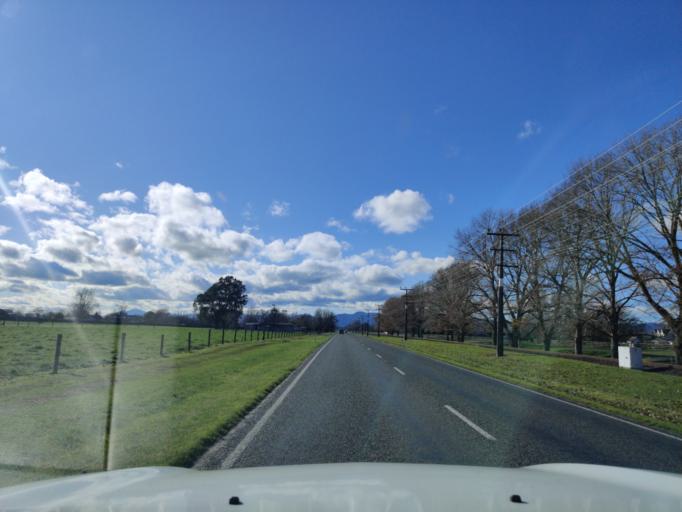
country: NZ
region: Waikato
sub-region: Matamata-Piako District
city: Matamata
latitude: -37.8437
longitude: 175.7624
